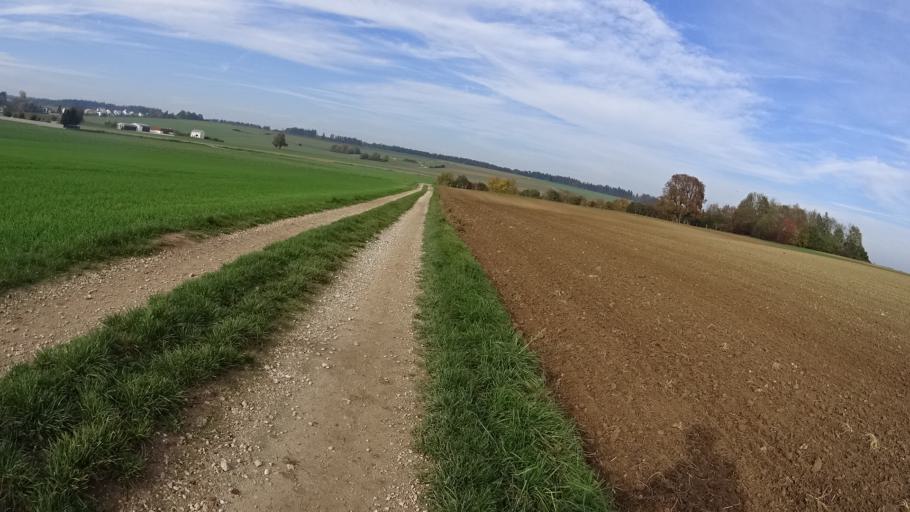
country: DE
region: Bavaria
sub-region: Upper Bavaria
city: Buxheim
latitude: 48.8228
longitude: 11.2839
